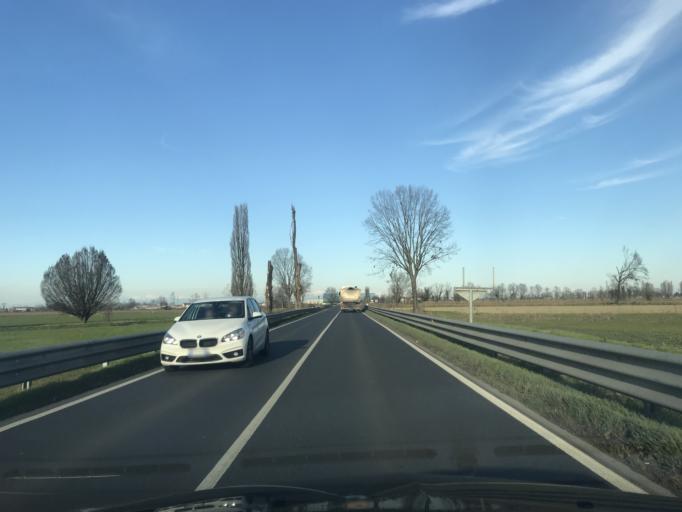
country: IT
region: Lombardy
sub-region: Provincia di Lodi
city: Borgo San Giovanni
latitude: 45.2601
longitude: 9.4340
